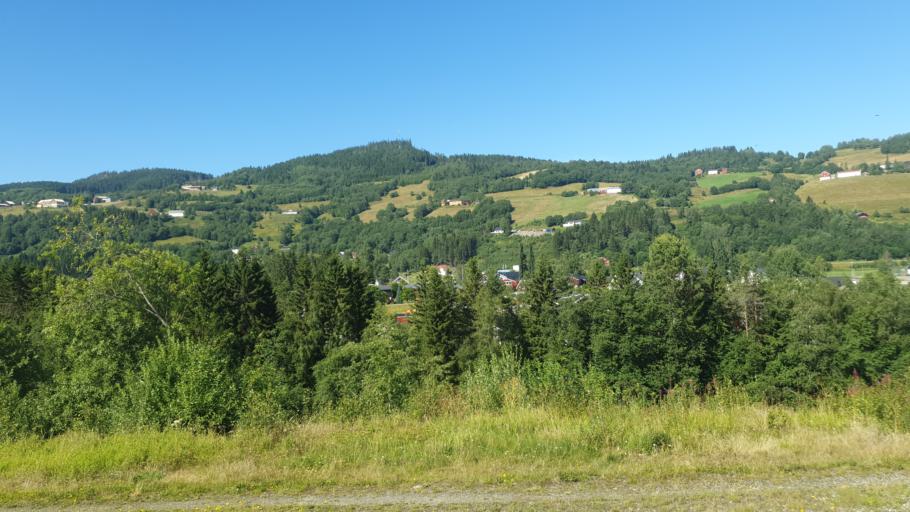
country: NO
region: Sor-Trondelag
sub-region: Meldal
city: Meldal
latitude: 63.1684
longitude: 9.7468
